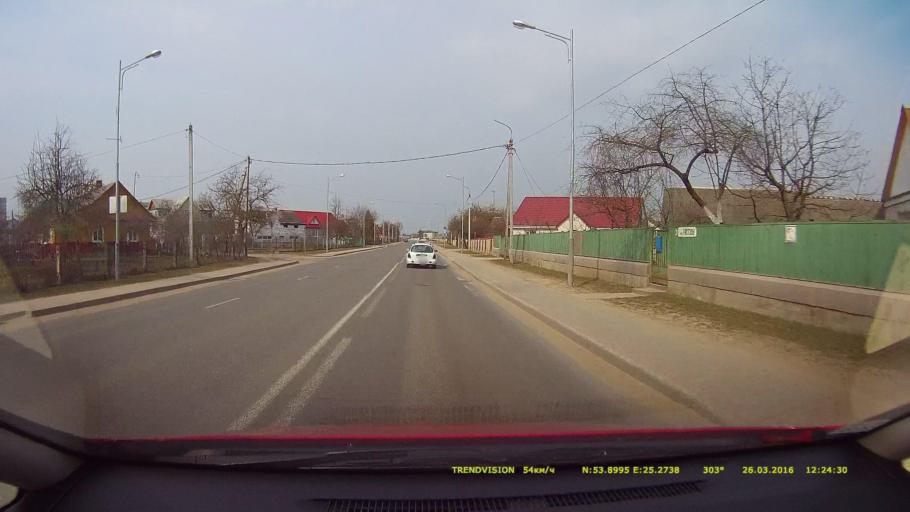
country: BY
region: Grodnenskaya
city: Lida
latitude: 53.8996
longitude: 25.2735
